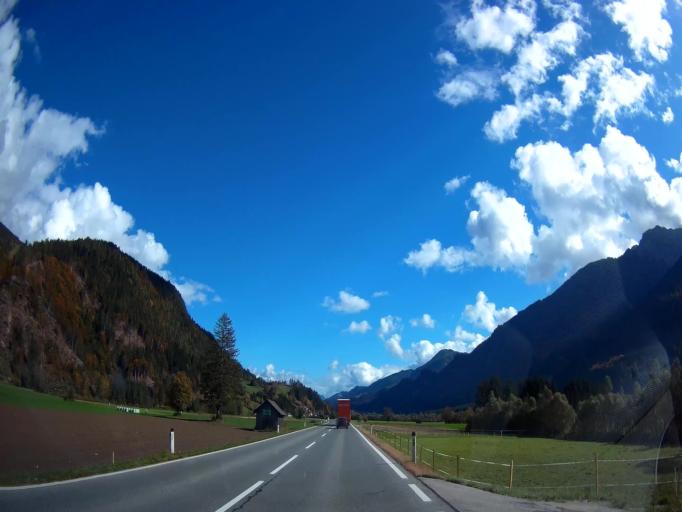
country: AT
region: Carinthia
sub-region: Politischer Bezirk Spittal an der Drau
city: Irschen
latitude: 46.7409
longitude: 13.0446
